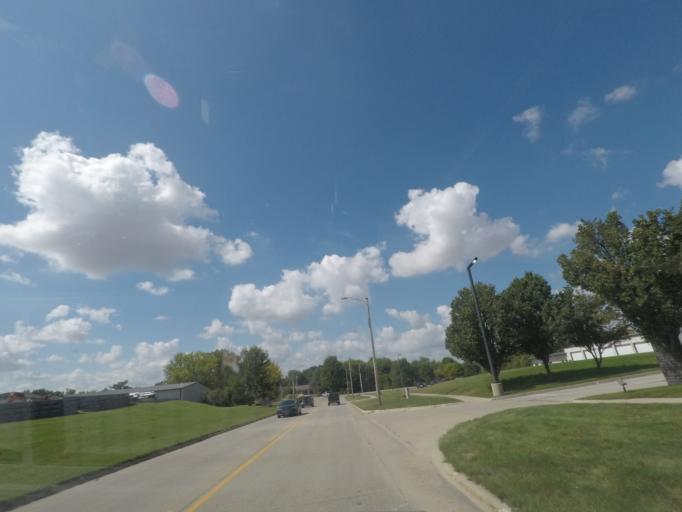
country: US
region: Iowa
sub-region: Story County
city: Nevada
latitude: 42.0098
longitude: -93.4428
